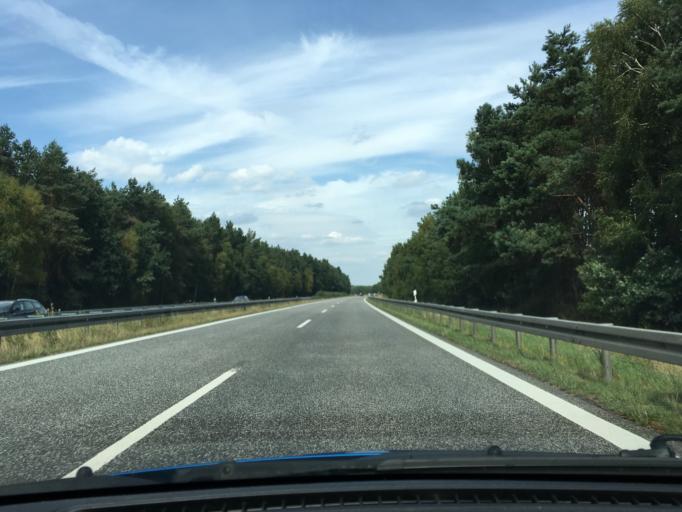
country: DE
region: Mecklenburg-Vorpommern
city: Mirow
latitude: 53.4989
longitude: 11.4758
